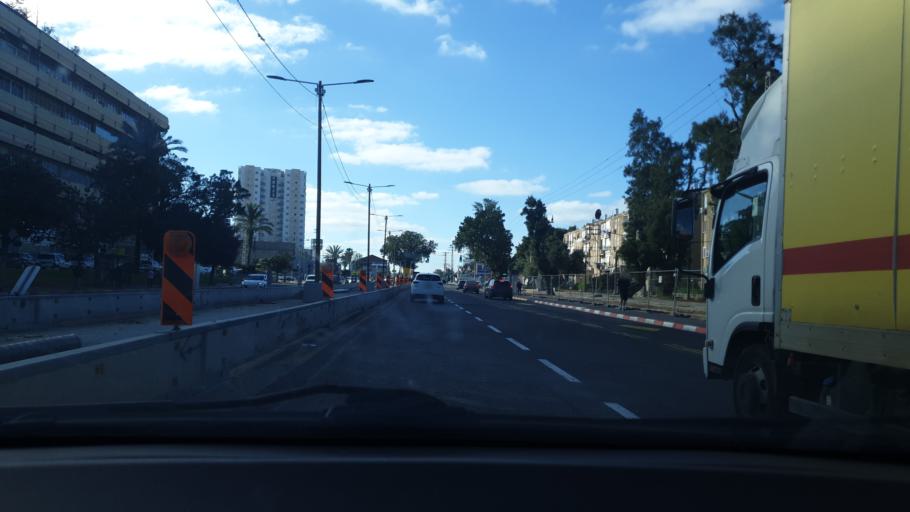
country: IL
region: Tel Aviv
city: Yafo
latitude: 32.0417
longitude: 34.7731
